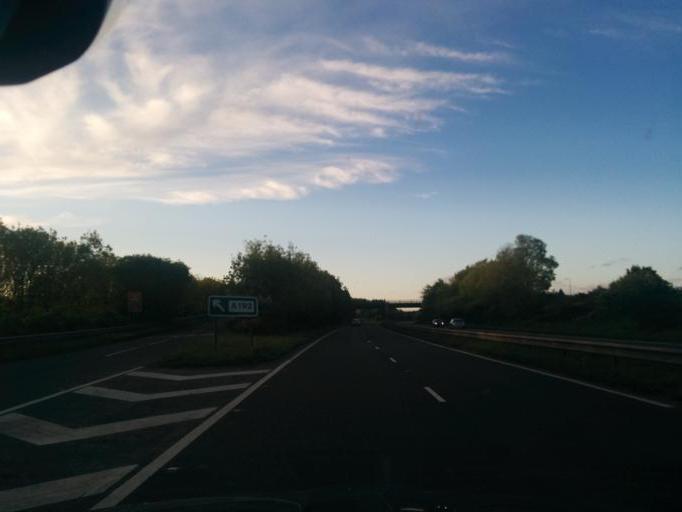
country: GB
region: England
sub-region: Northumberland
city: Cramlington
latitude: 55.1022
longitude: -1.5666
